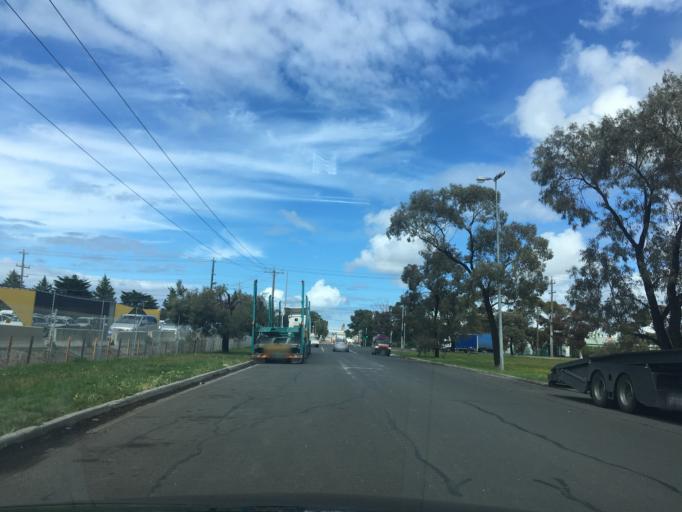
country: AU
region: Victoria
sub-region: Hobsons Bay
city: Altona
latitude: -37.8456
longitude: 144.8045
